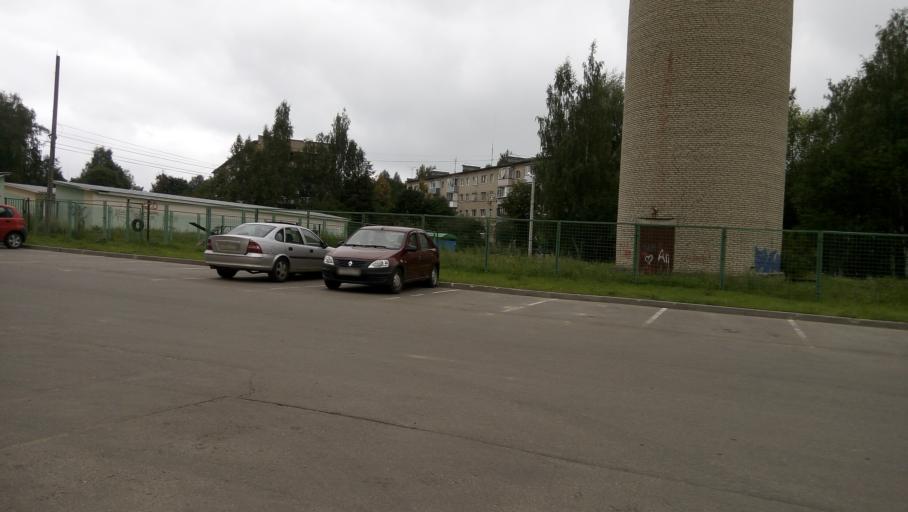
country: RU
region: Moskovskaya
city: Zelenogradskiy
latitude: 56.0908
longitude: 37.9003
